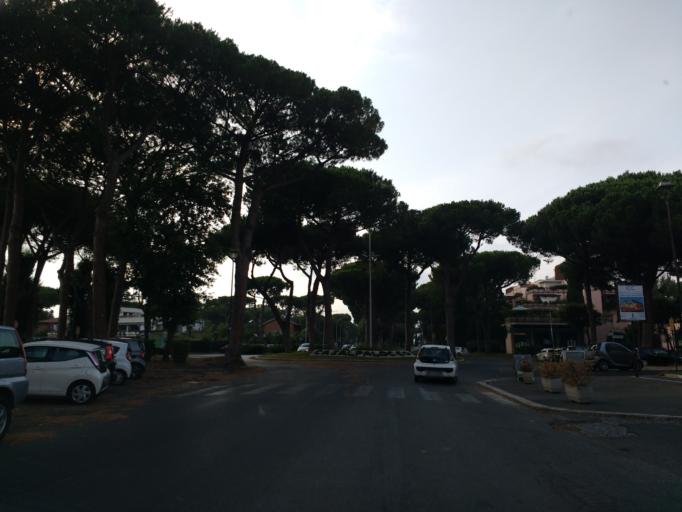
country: IT
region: Latium
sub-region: Citta metropolitana di Roma Capitale
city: Acilia-Castel Fusano-Ostia Antica
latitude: 41.7468
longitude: 12.3563
